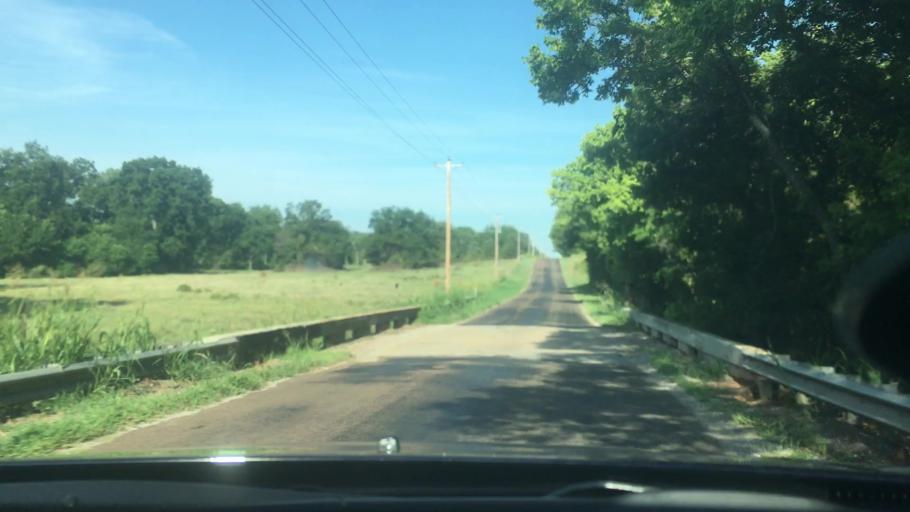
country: US
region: Oklahoma
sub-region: Garvin County
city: Pauls Valley
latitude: 34.6521
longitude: -97.3620
